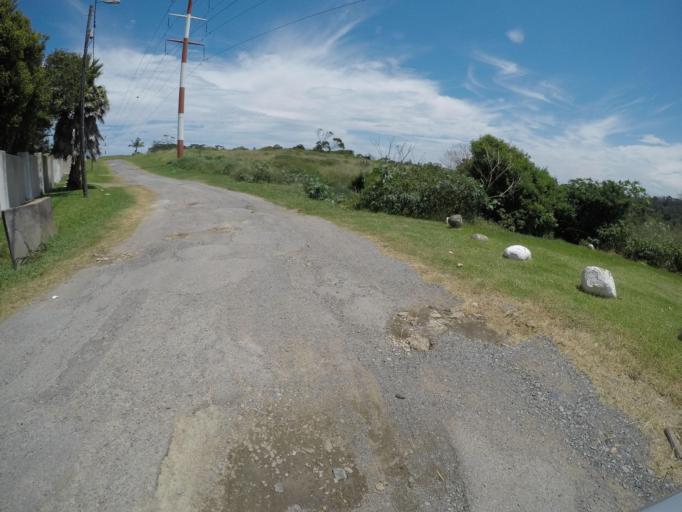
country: ZA
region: Eastern Cape
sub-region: Buffalo City Metropolitan Municipality
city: East London
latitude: -33.0320
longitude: 27.8482
